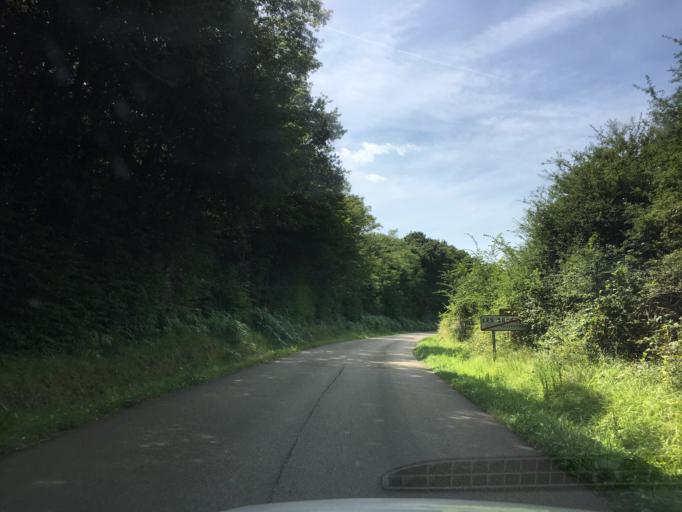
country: FR
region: Bourgogne
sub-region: Departement de l'Yonne
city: Charbuy
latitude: 47.7982
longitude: 3.4618
